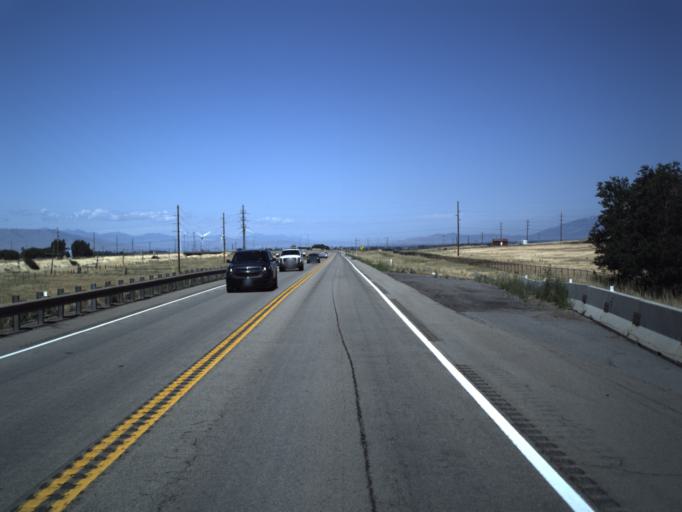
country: US
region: Utah
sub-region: Utah County
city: Mapleton
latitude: 40.0769
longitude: -111.5820
